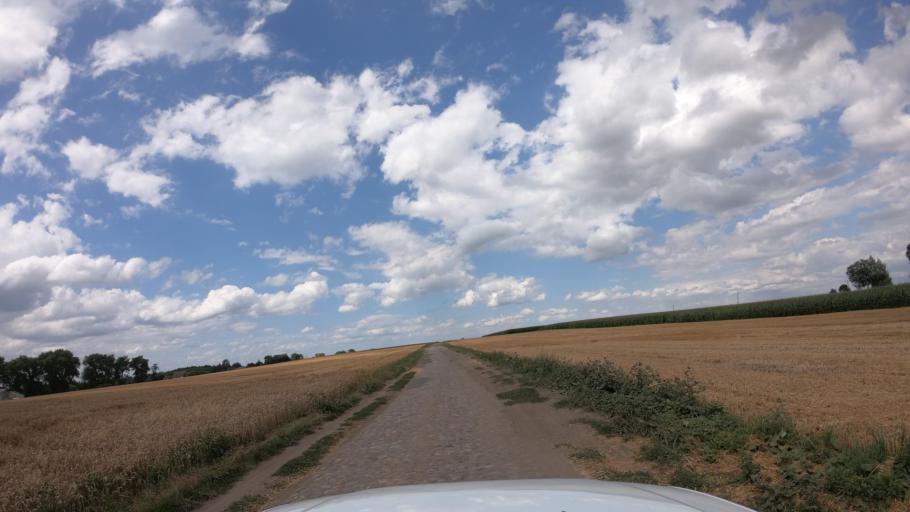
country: PL
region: West Pomeranian Voivodeship
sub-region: Powiat pyrzycki
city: Warnice
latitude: 53.2399
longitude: 14.9139
